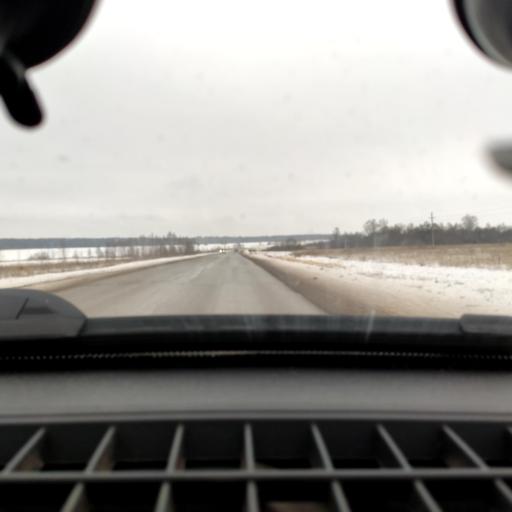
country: RU
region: Bashkortostan
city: Iglino
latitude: 54.7931
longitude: 56.4165
